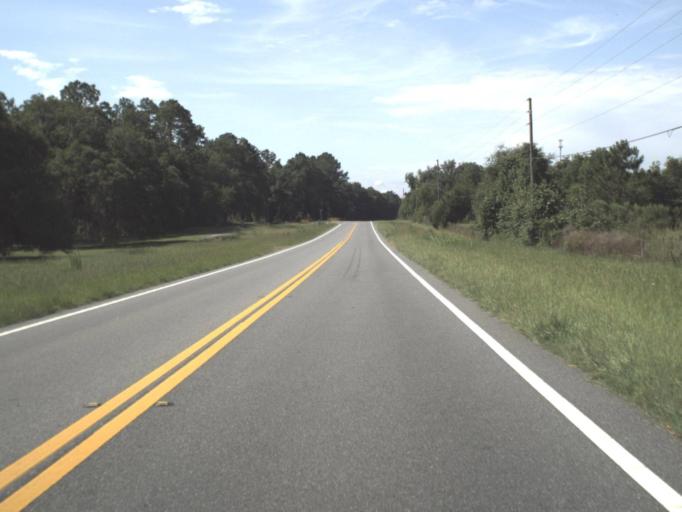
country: US
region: Florida
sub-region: Madison County
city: Madison
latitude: 30.5345
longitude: -83.3675
